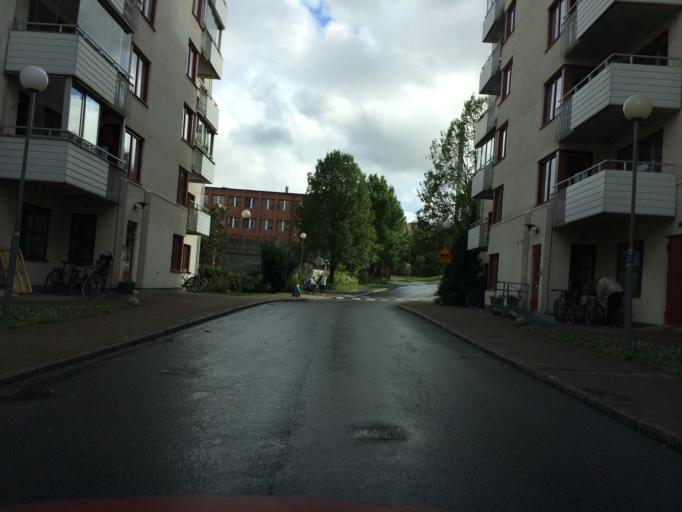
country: SE
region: Stockholm
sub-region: Stockholms Kommun
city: Bromma
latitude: 59.3073
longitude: 17.9810
